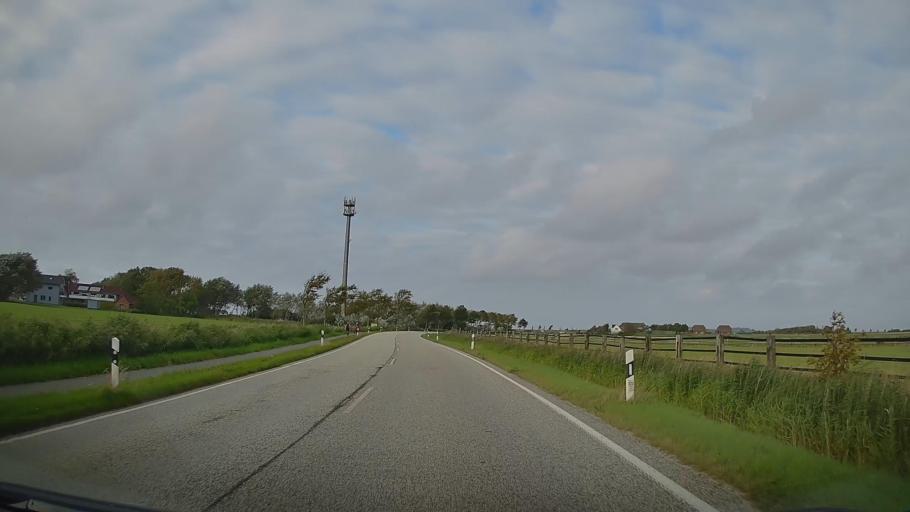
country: DE
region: Schleswig-Holstein
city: Sankt Peter-Ording
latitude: 54.3278
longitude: 8.6139
